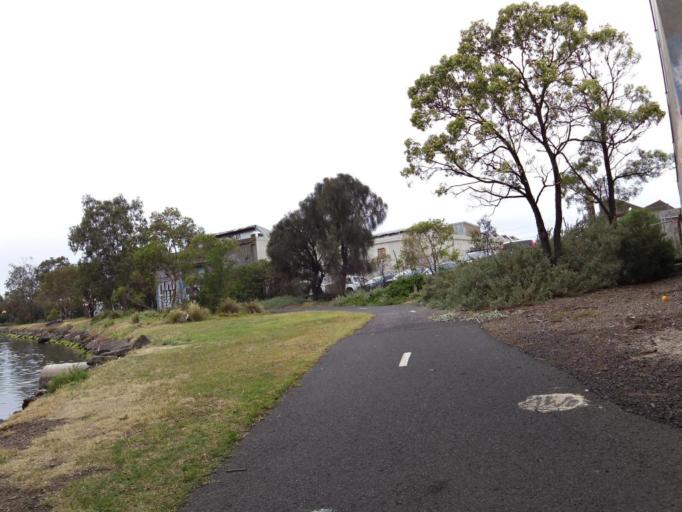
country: AU
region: Victoria
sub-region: Melbourne
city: Ascot Vale
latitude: -37.7983
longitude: 144.9169
